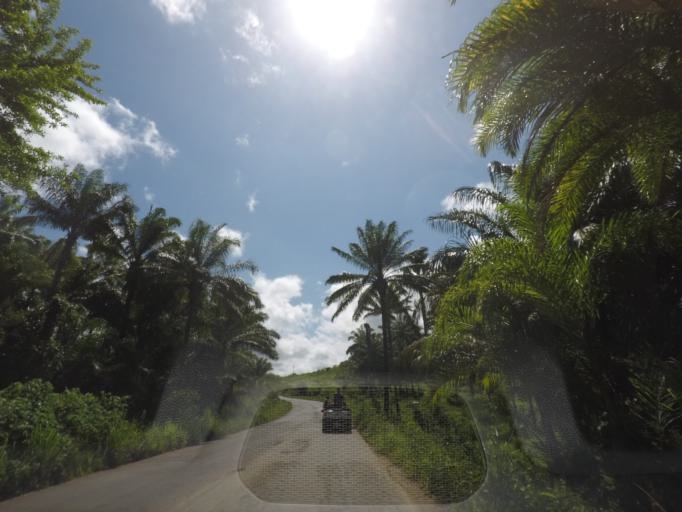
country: BR
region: Bahia
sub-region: Taperoa
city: Taperoa
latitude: -13.5154
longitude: -39.0952
